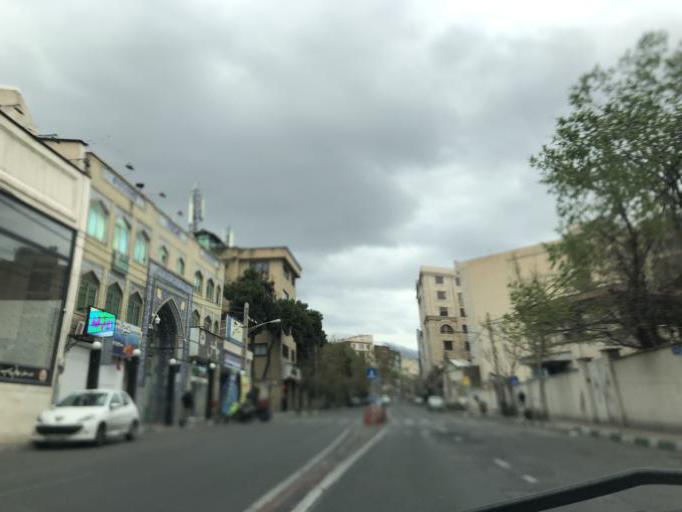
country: IR
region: Tehran
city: Tajrish
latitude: 35.7776
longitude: 51.4429
